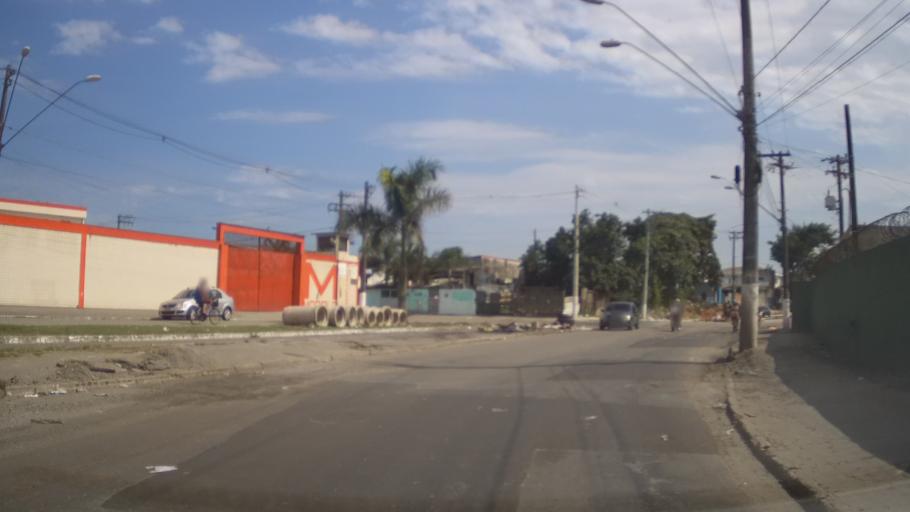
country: BR
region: Sao Paulo
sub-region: Praia Grande
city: Praia Grande
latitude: -24.0038
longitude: -46.4361
